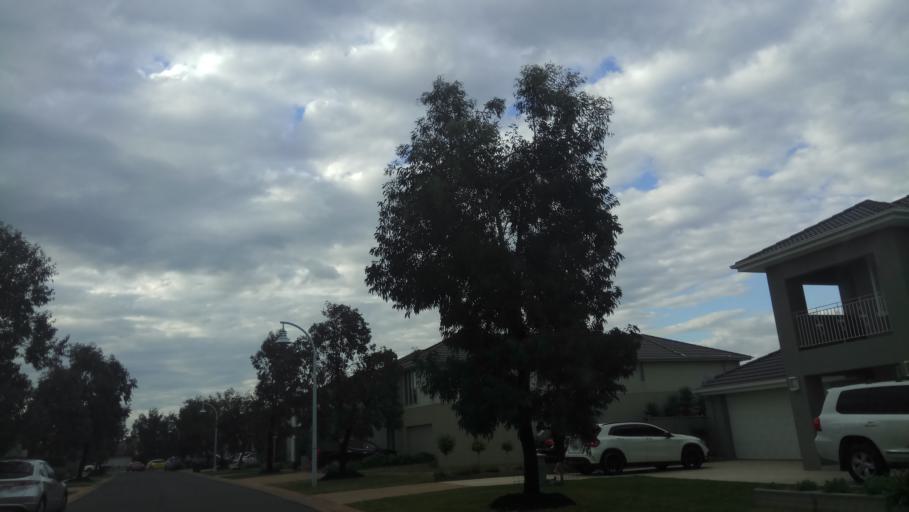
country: AU
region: Victoria
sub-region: Hobsons Bay
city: Altona Meadows
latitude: -37.8998
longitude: 144.7799
